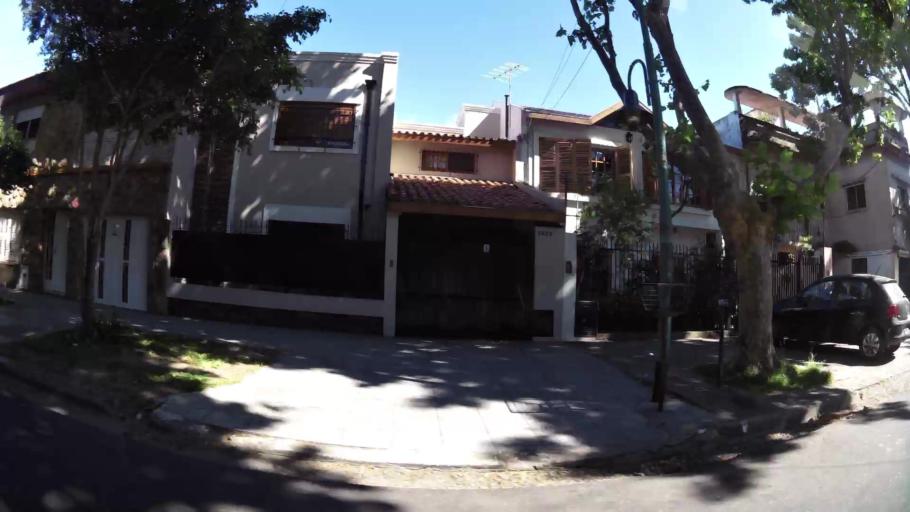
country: AR
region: Buenos Aires
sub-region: Partido de General San Martin
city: General San Martin
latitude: -34.5350
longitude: -58.5141
